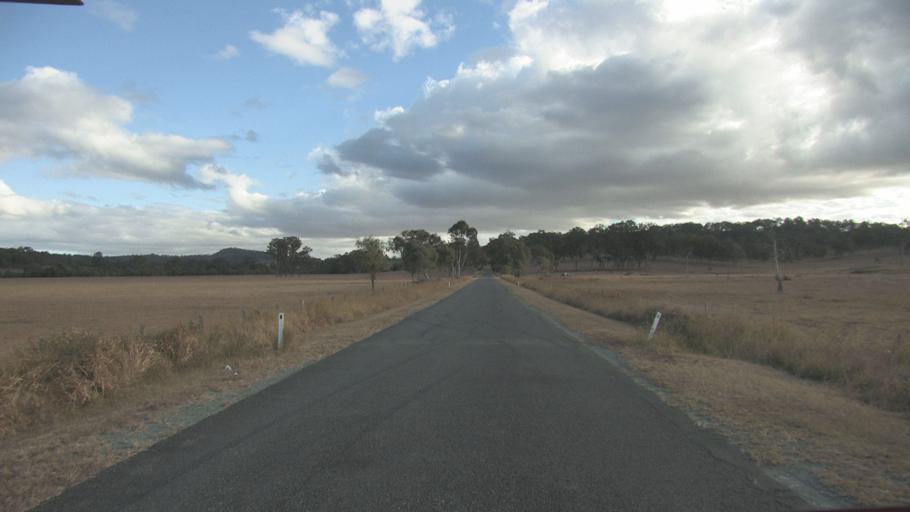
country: AU
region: Queensland
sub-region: Logan
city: Cedar Vale
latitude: -27.8878
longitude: 153.0718
